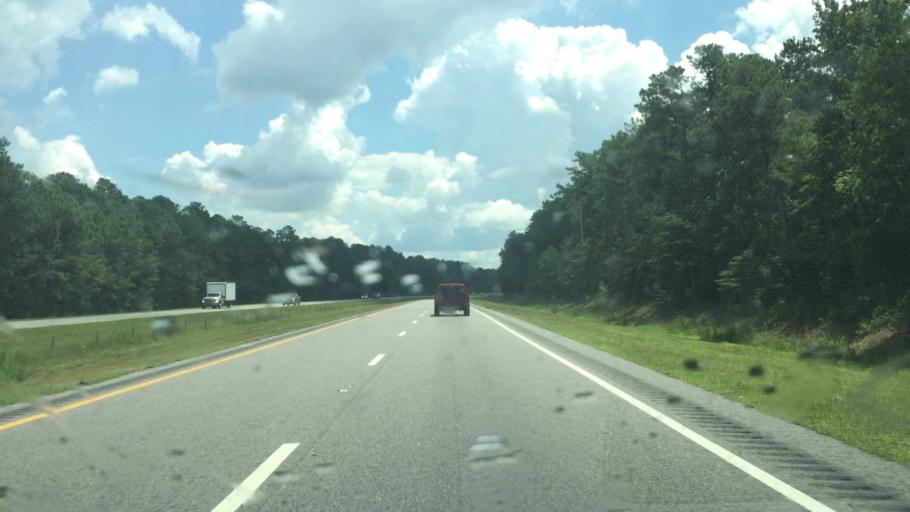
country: US
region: North Carolina
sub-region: Columbus County
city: Chadbourn
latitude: 34.3825
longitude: -78.8598
